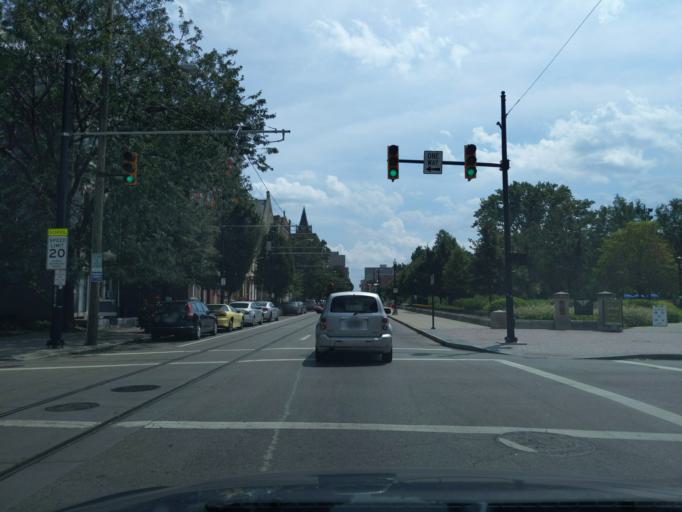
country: US
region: Kentucky
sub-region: Kenton County
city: Covington
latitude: 39.1104
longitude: -84.5170
